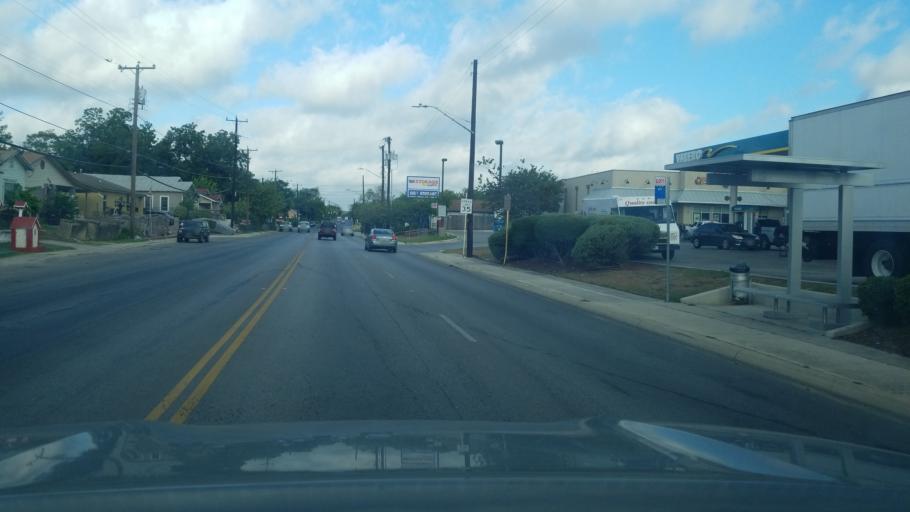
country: US
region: Texas
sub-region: Bexar County
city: San Antonio
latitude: 29.4121
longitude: -98.5157
